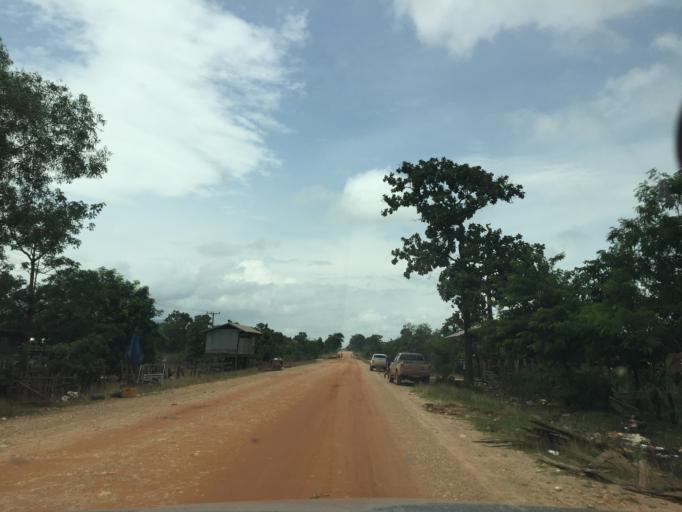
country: LA
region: Attapu
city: Attapu
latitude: 14.6859
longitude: 106.5959
